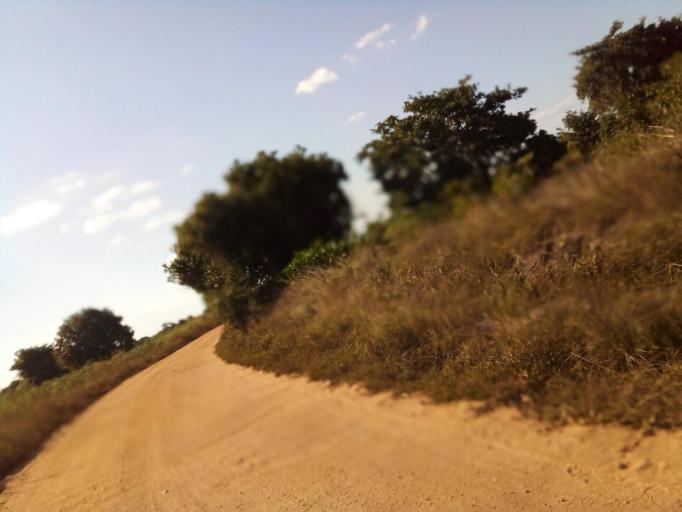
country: MZ
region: Zambezia
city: Quelimane
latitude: -17.5608
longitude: 36.6358
